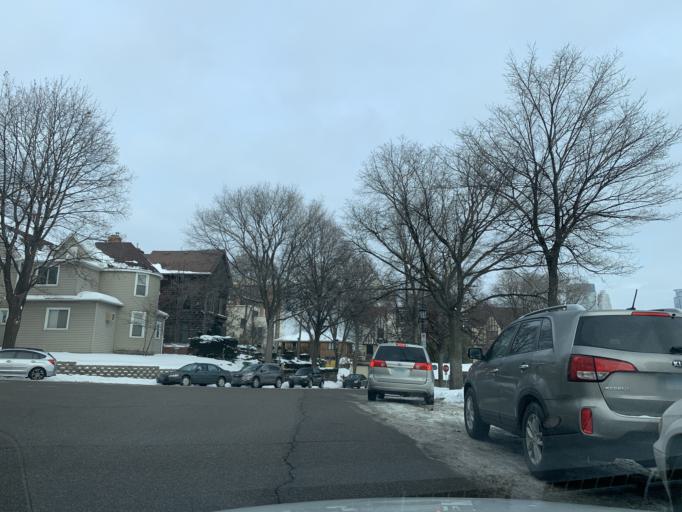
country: US
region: Minnesota
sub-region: Hennepin County
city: Minneapolis
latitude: 44.9635
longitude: -93.2808
